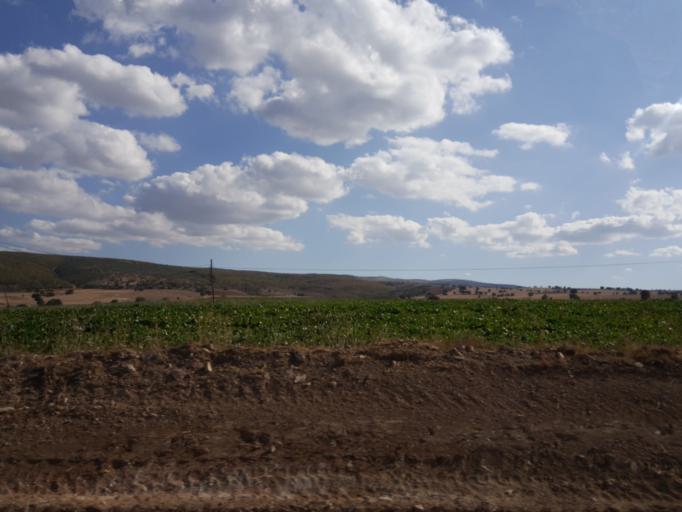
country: TR
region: Tokat
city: Sulusaray
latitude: 40.0040
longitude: 36.1424
